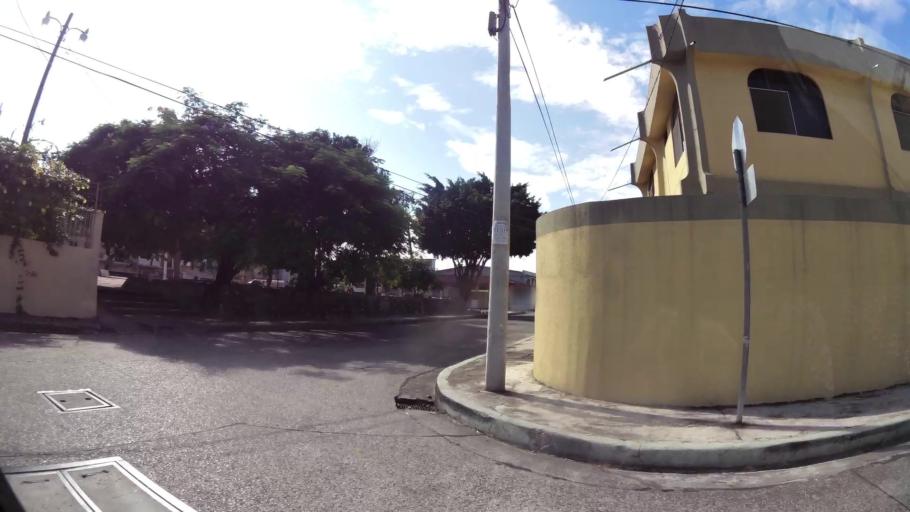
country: EC
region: Guayas
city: Guayaquil
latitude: -2.2267
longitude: -79.8937
